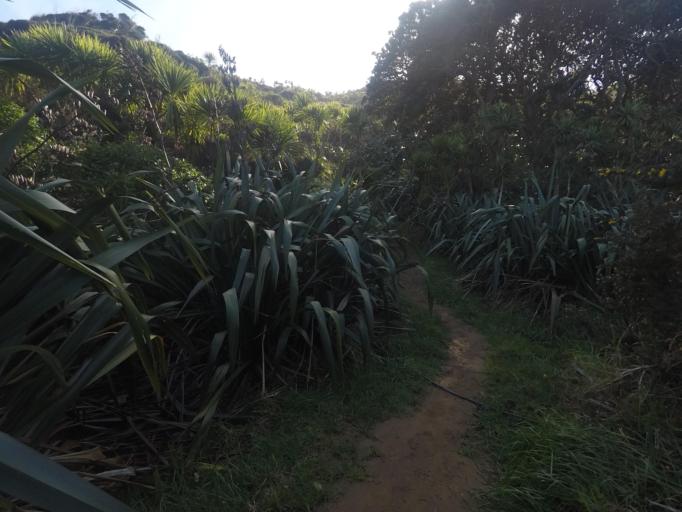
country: NZ
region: Auckland
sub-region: Auckland
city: Muriwai Beach
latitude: -36.8599
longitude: 174.4343
